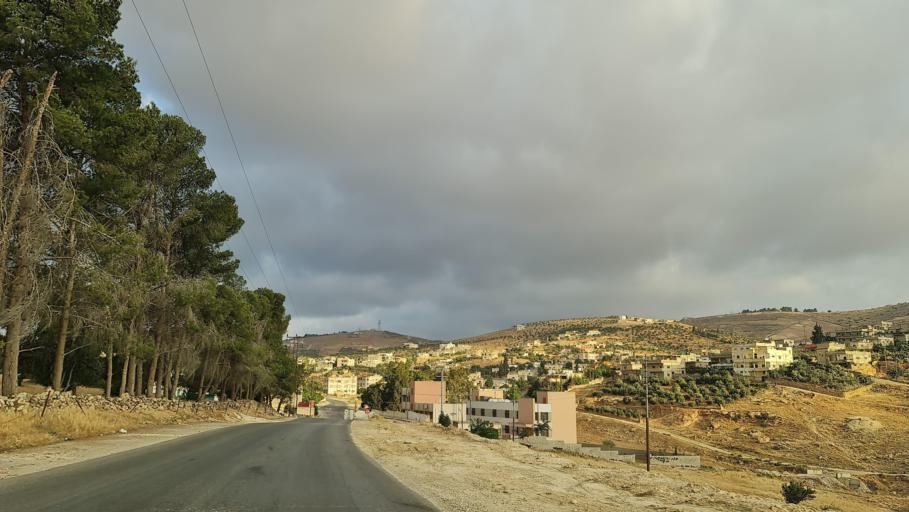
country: JO
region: Amman
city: Al Jubayhah
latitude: 32.0920
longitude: 35.9297
